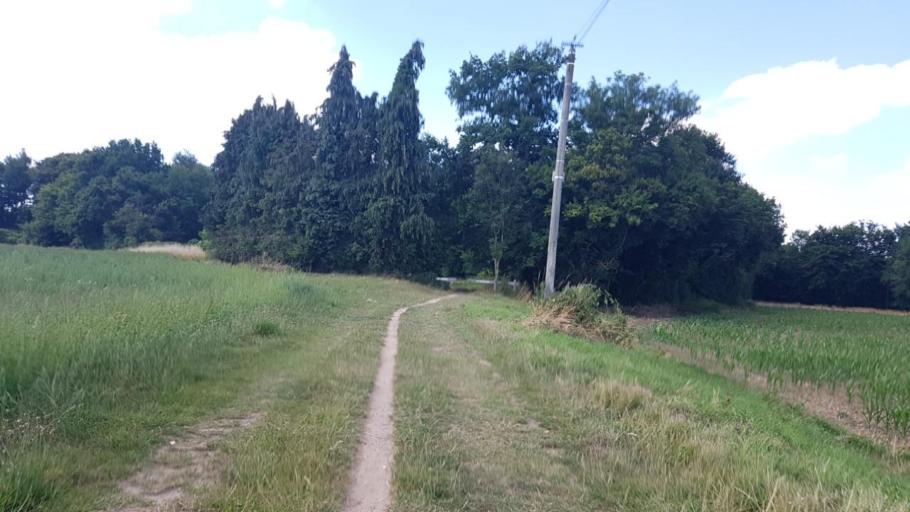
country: FR
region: Picardie
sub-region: Departement de l'Oise
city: Ver-sur-Launette
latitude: 49.1115
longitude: 2.6795
